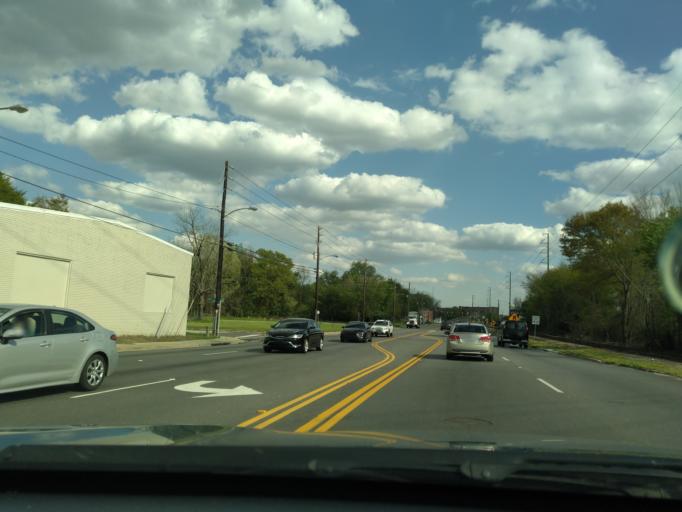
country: US
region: South Carolina
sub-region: Florence County
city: Florence
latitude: 34.2046
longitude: -79.7685
